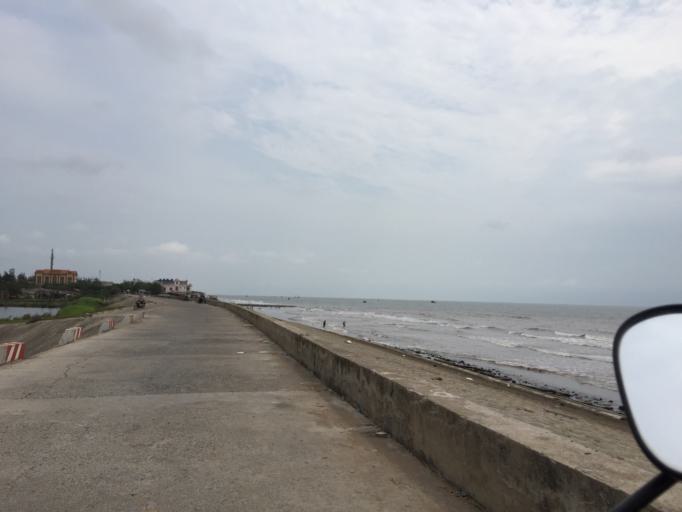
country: VN
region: Ninh Binh
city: Thi Tran Phat Diem
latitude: 20.0203
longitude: 106.2154
